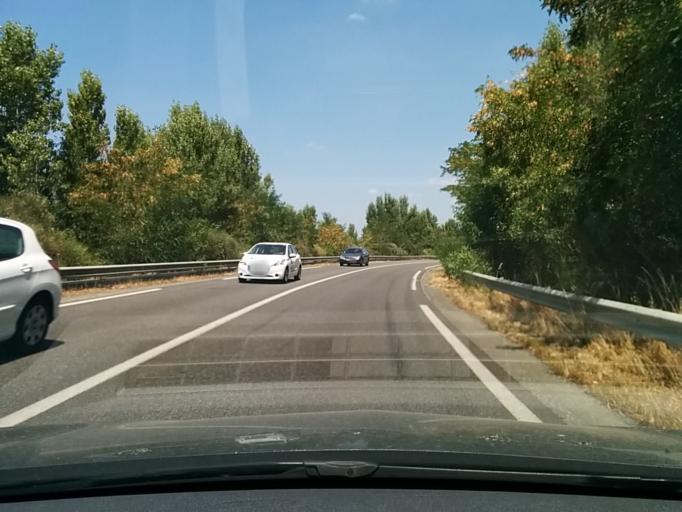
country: FR
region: Midi-Pyrenees
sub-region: Departement de la Haute-Garonne
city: Labege
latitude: 43.5264
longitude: 1.5216
